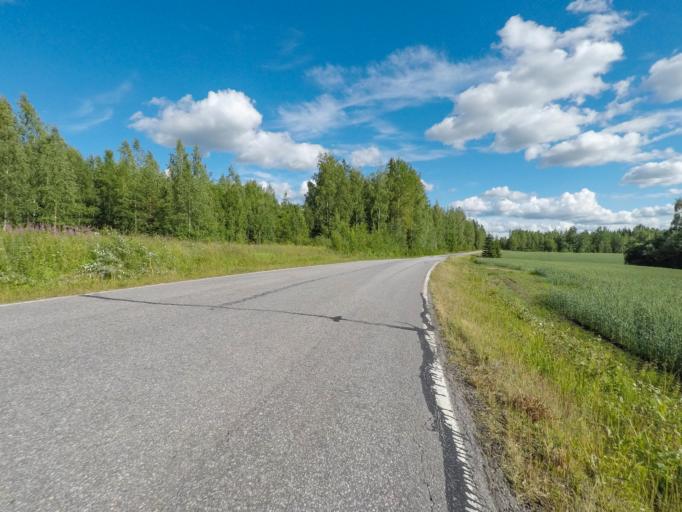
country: FI
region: South Karelia
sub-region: Imatra
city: Imatra
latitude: 61.1341
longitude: 28.6596
